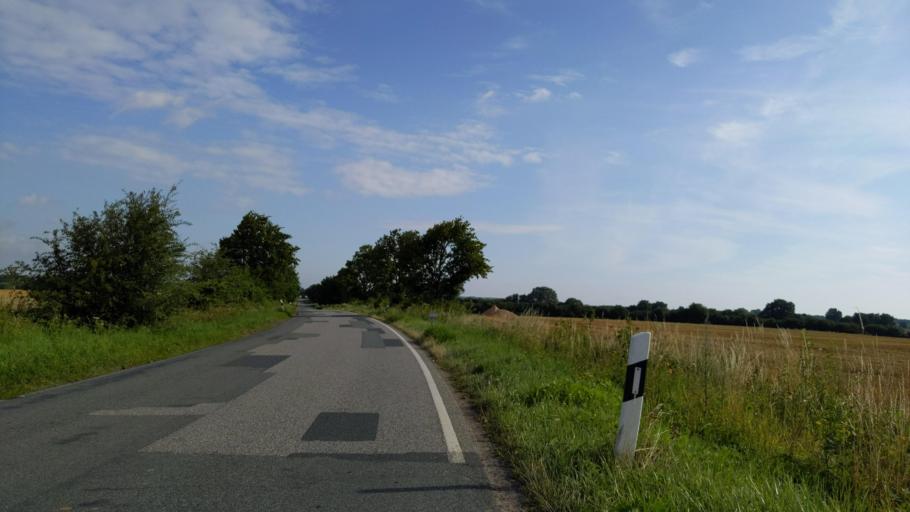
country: DE
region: Schleswig-Holstein
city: Bad Schwartau
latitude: 53.9759
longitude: 10.6563
